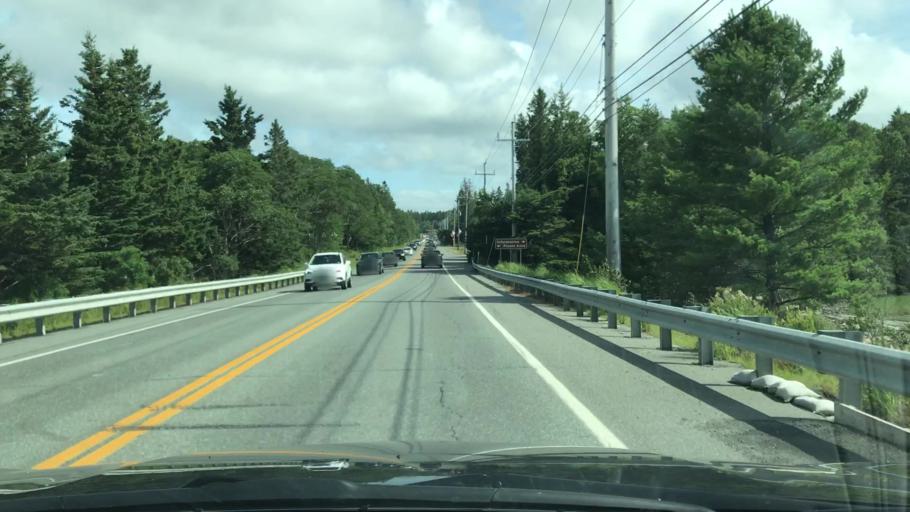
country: US
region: Maine
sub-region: Hancock County
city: Trenton
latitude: 44.4288
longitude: -68.3670
